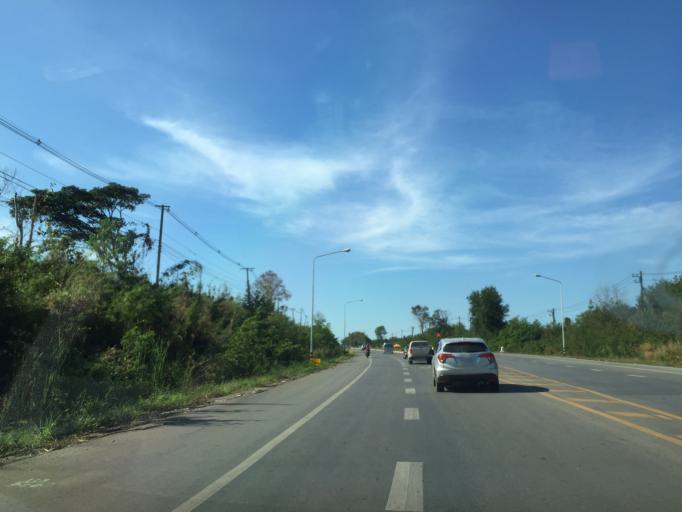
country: TH
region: Loei
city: Wang Saphung
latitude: 17.2930
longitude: 101.8199
